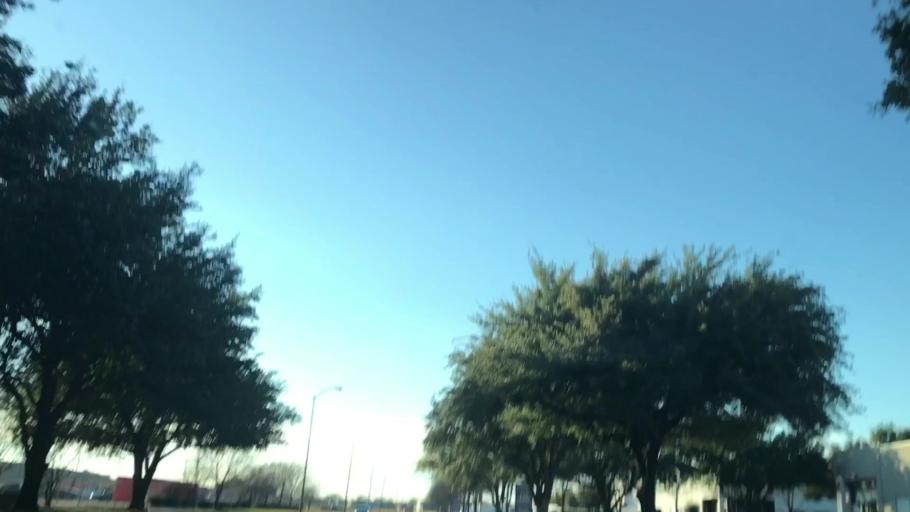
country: US
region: Texas
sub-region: Dallas County
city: Balch Springs
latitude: 32.7843
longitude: -96.6772
